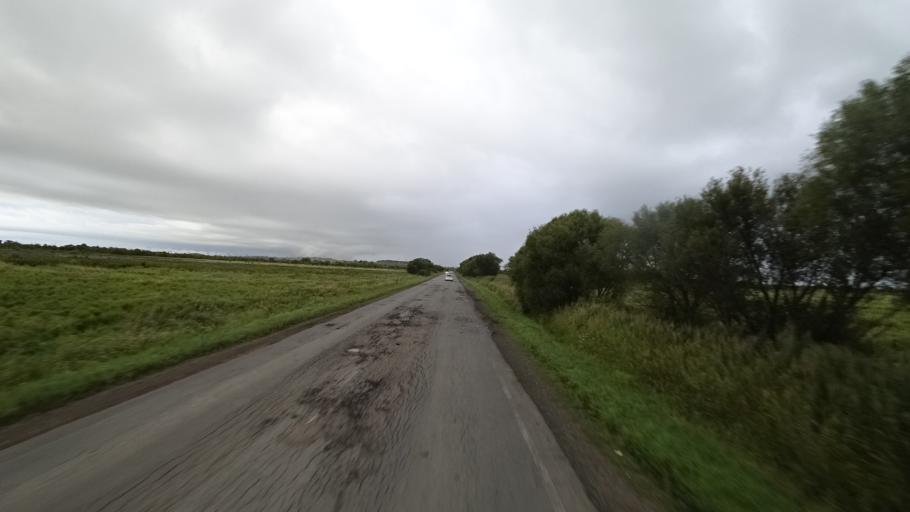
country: RU
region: Primorskiy
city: Chernigovka
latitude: 44.3582
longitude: 132.5593
